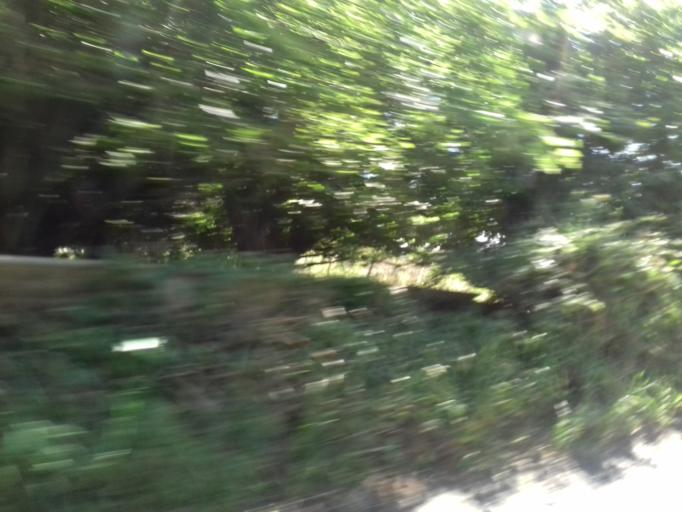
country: IE
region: Leinster
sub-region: Fingal County
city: Swords
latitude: 53.5111
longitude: -6.2677
